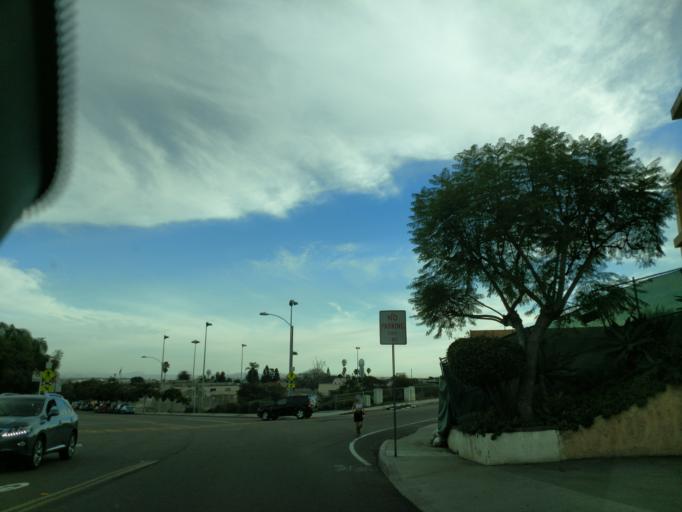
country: US
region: California
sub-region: San Diego County
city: Coronado
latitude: 32.7229
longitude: -117.2340
